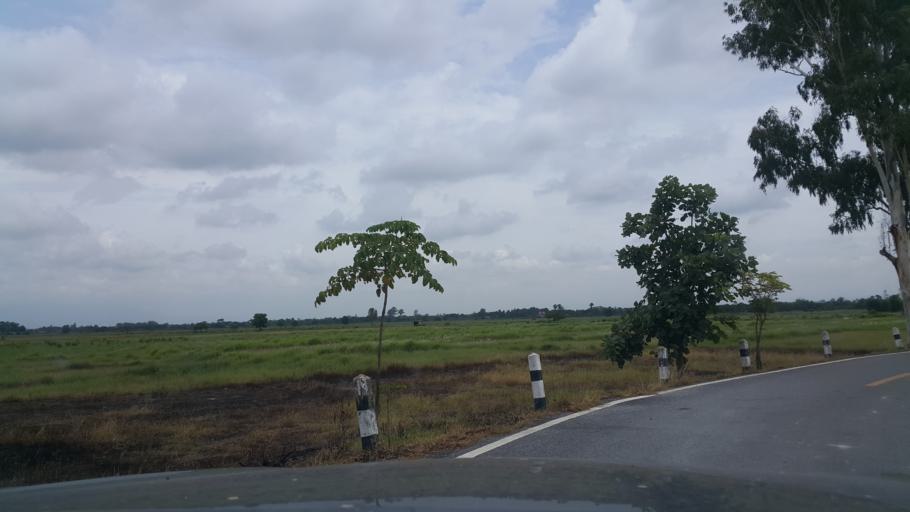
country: TH
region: Lamphun
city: Ban Thi
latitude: 18.6483
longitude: 99.1467
